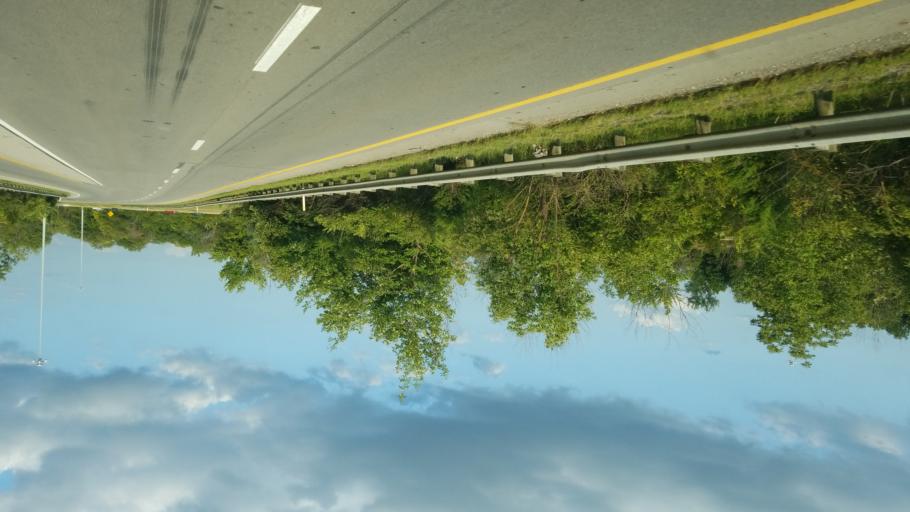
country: US
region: Ohio
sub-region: Franklin County
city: Grove City
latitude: 39.8900
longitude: -83.0378
